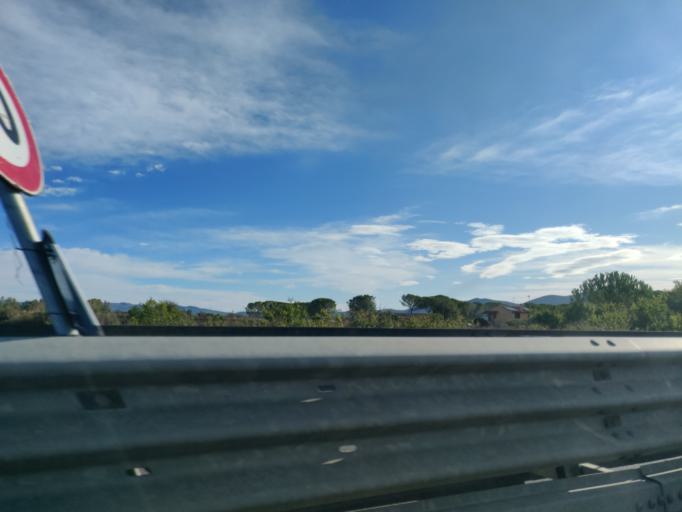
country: IT
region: Tuscany
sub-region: Provincia di Grosseto
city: Braccagni
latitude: 42.8984
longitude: 11.0497
